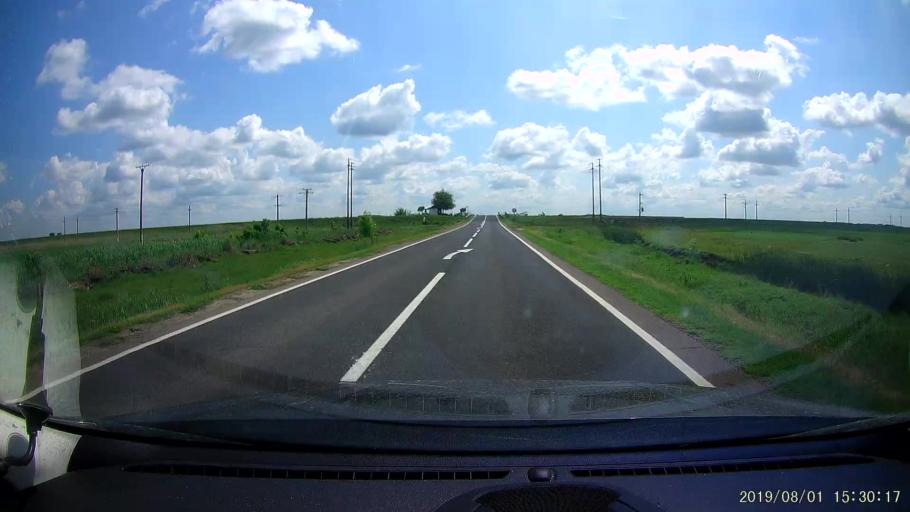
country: RO
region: Braila
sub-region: Comuna Viziru
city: Viziru
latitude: 44.9661
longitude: 27.6803
